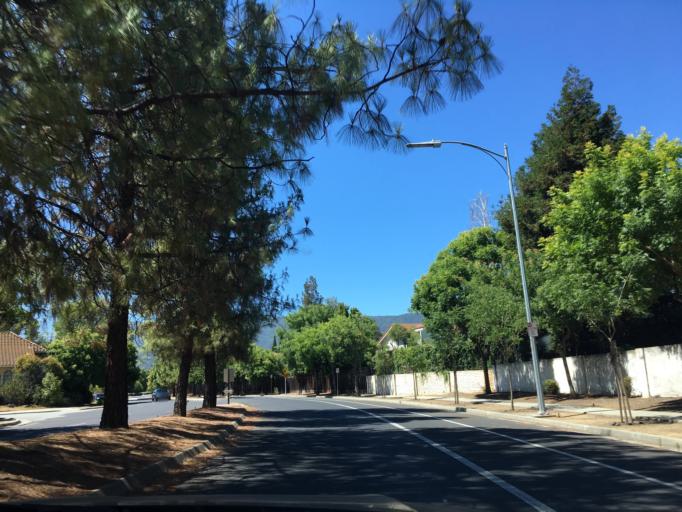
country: US
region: California
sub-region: Santa Clara County
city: Cambrian Park
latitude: 37.2354
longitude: -121.8754
